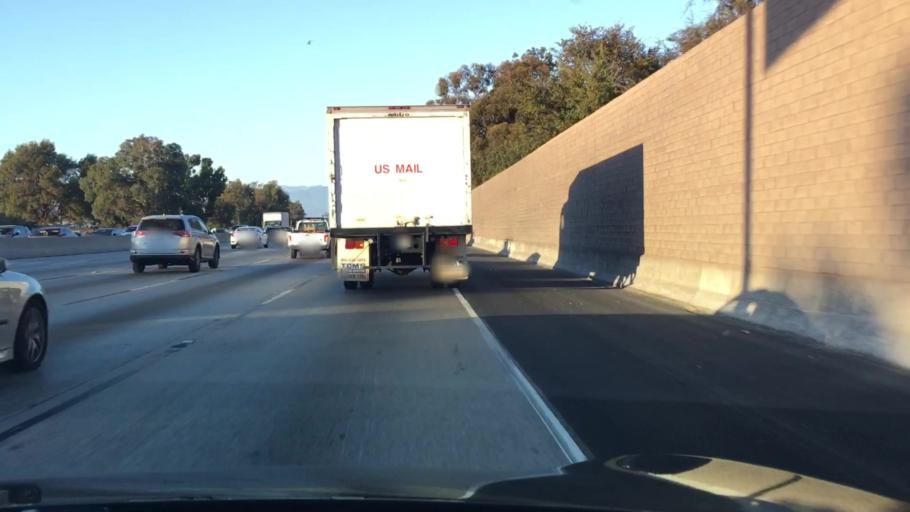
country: US
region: California
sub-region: Los Angeles County
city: Santa Fe Springs
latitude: 33.9548
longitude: -118.0888
